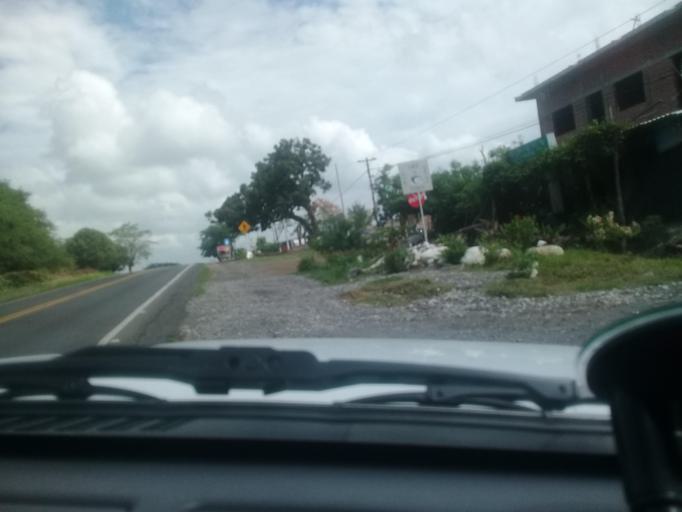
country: MX
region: Veracruz
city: Paso de Ovejas
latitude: 19.2733
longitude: -96.4205
